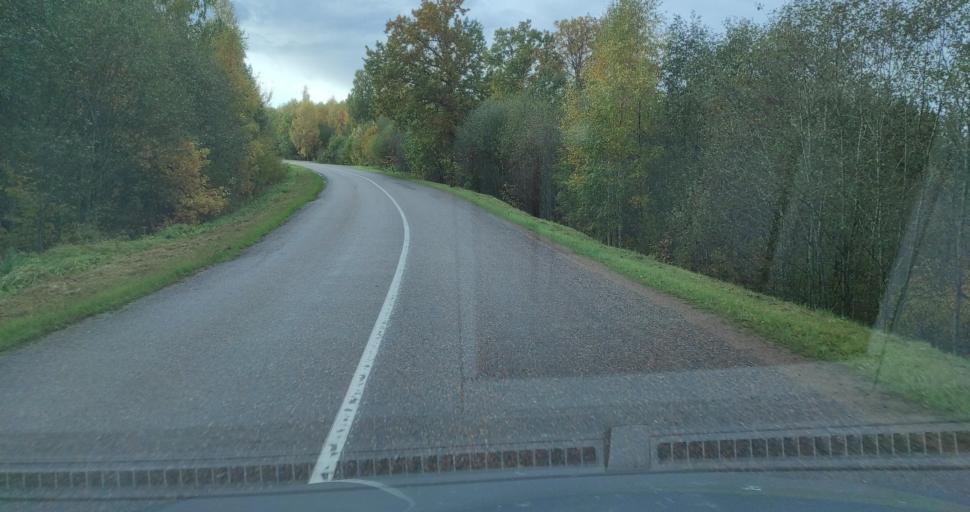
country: LV
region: Skrunda
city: Skrunda
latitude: 56.5977
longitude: 21.9034
